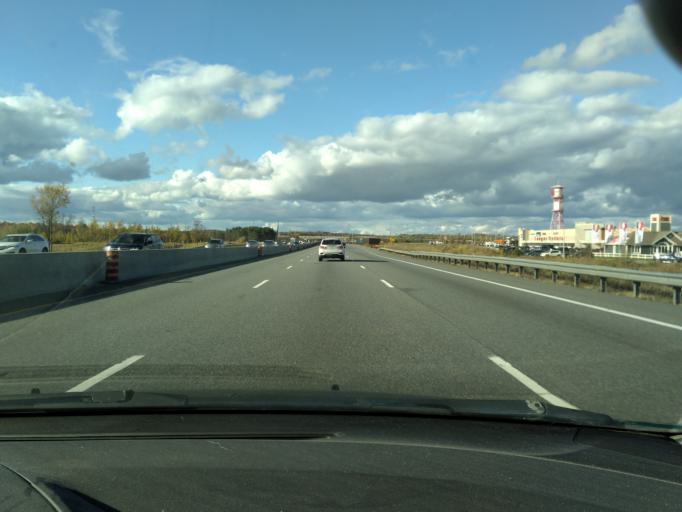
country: CA
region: Ontario
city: Bradford West Gwillimbury
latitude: 44.1955
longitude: -79.6520
